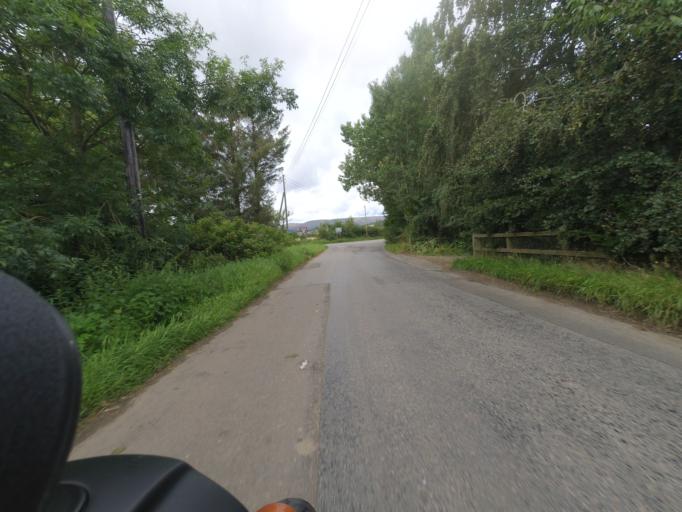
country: GB
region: Scotland
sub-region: Aberdeenshire
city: Laurencekirk
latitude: 56.8408
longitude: -2.5673
